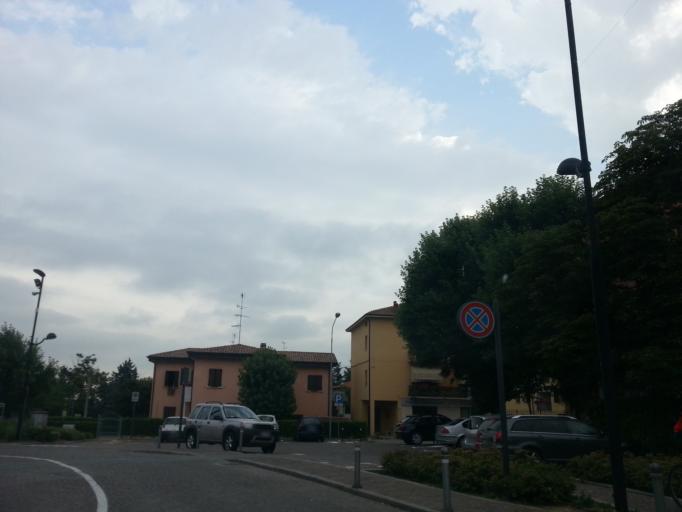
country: IT
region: Emilia-Romagna
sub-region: Provincia di Reggio Emilia
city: Albinea
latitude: 44.6198
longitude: 10.6028
